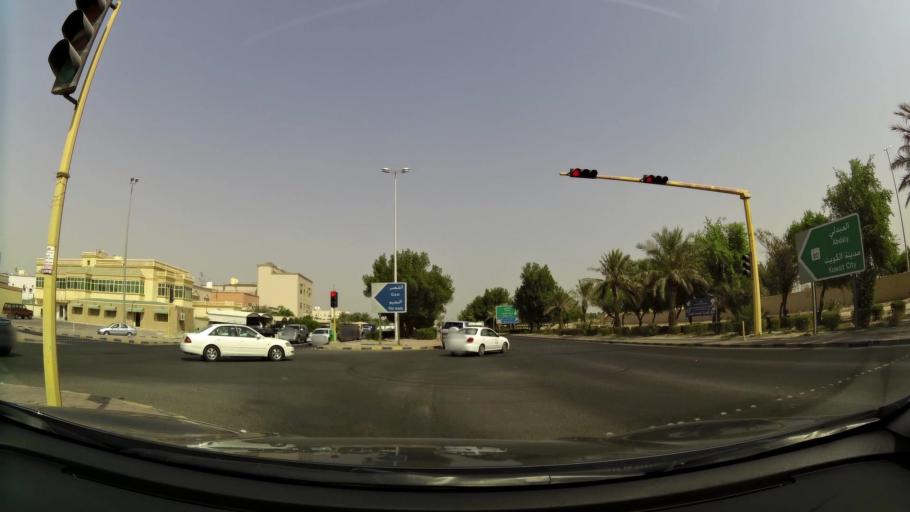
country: KW
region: Muhafazat al Jahra'
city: Al Jahra'
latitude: 29.3316
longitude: 47.7061
